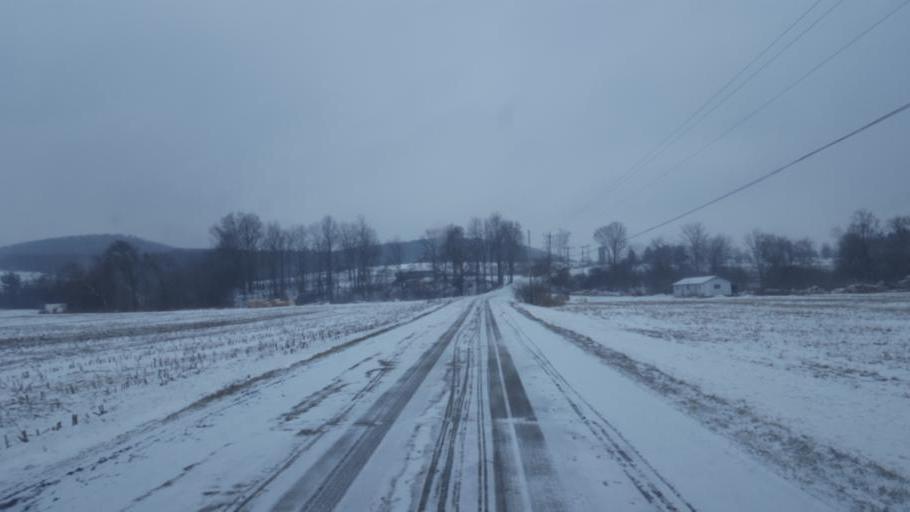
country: US
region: Pennsylvania
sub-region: Tioga County
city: Elkland
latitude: 42.1023
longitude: -77.4613
